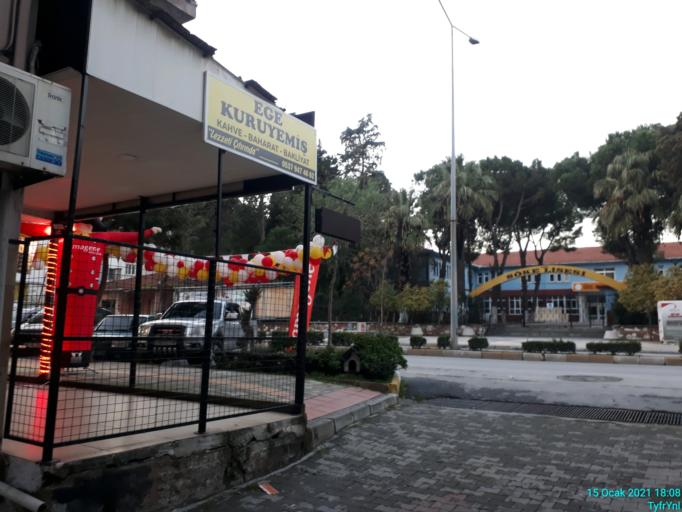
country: TR
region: Aydin
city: Soeke
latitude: 37.7598
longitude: 27.4117
